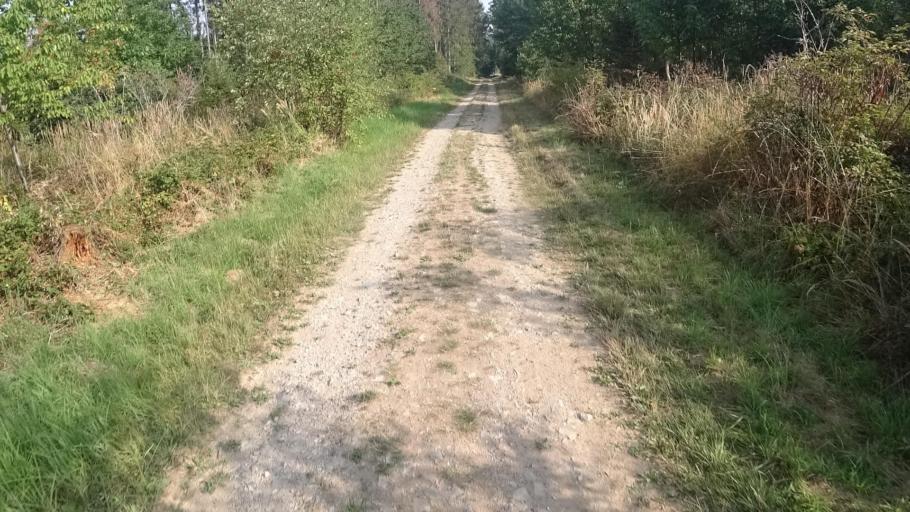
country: DE
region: Rheinland-Pfalz
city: Sargenroth
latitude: 49.9454
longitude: 7.5199
